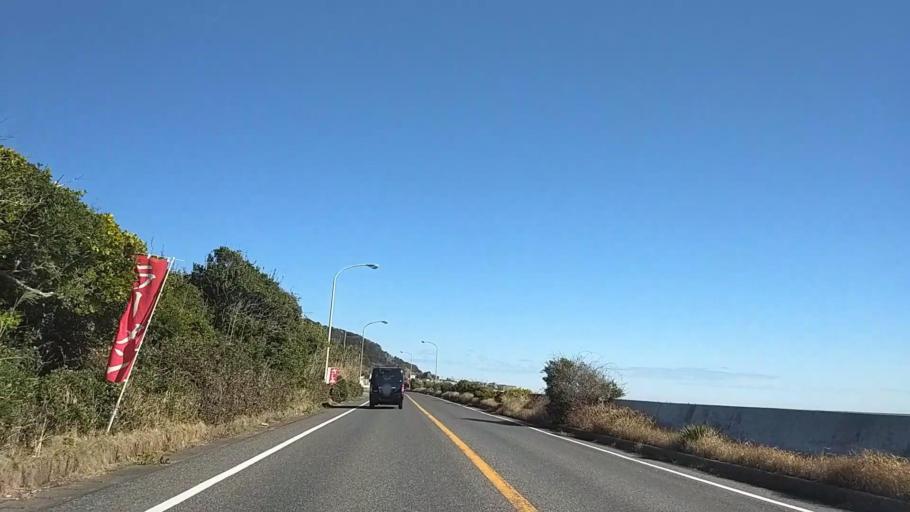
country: JP
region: Chiba
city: Kawaguchi
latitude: 35.0321
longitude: 140.0042
